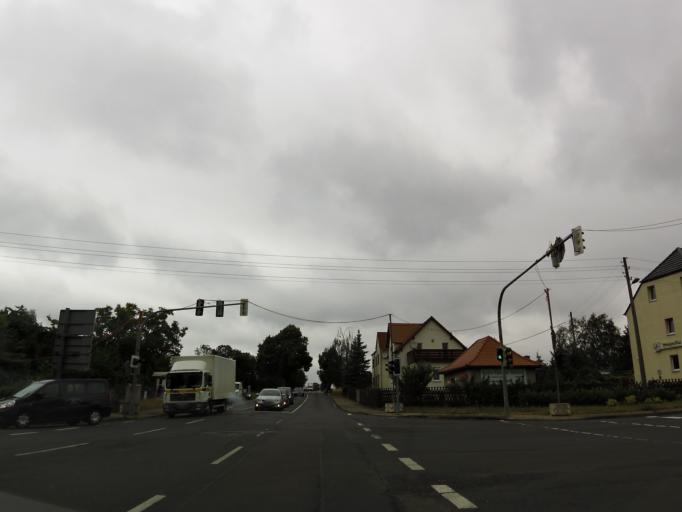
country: DE
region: Saxony
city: Markkleeberg
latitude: 51.2776
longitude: 12.4319
